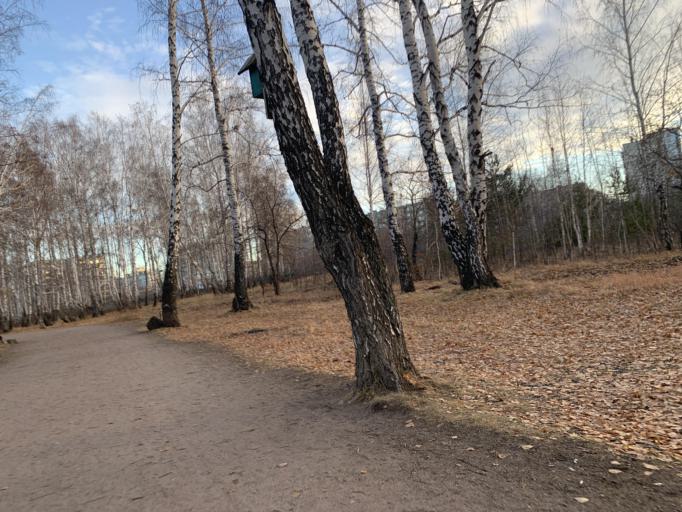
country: RU
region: Chelyabinsk
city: Roshchino
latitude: 55.2006
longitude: 61.3086
